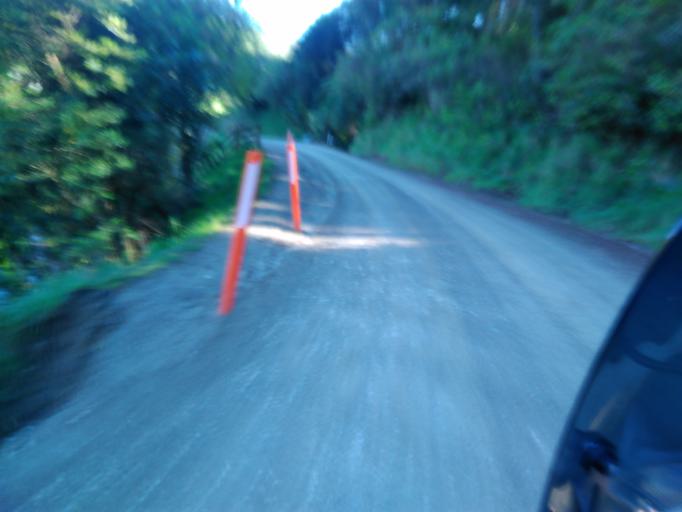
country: NZ
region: Gisborne
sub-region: Gisborne District
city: Gisborne
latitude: -38.3751
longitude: 177.6127
